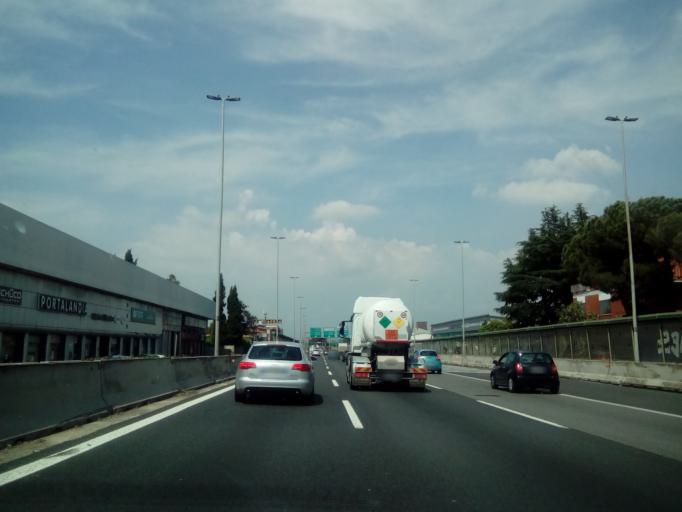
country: IT
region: Latium
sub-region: Citta metropolitana di Roma Capitale
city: Ciampino
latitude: 41.8301
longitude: 12.5853
